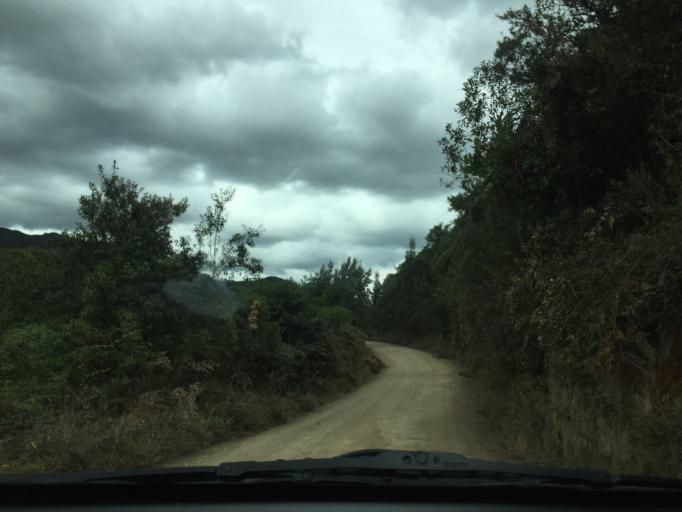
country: CO
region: Cundinamarca
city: Tabio
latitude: 4.9213
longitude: -74.1087
